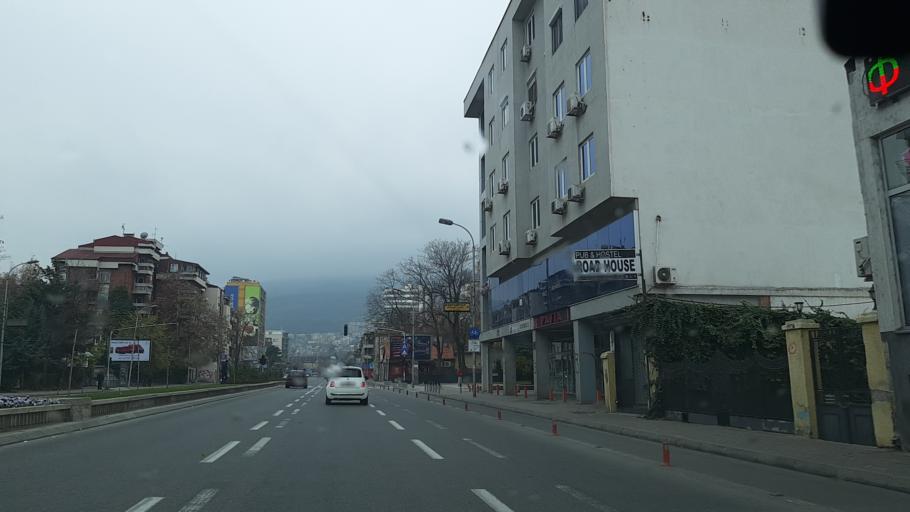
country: MK
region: Karpos
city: Skopje
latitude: 41.9975
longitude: 21.4252
